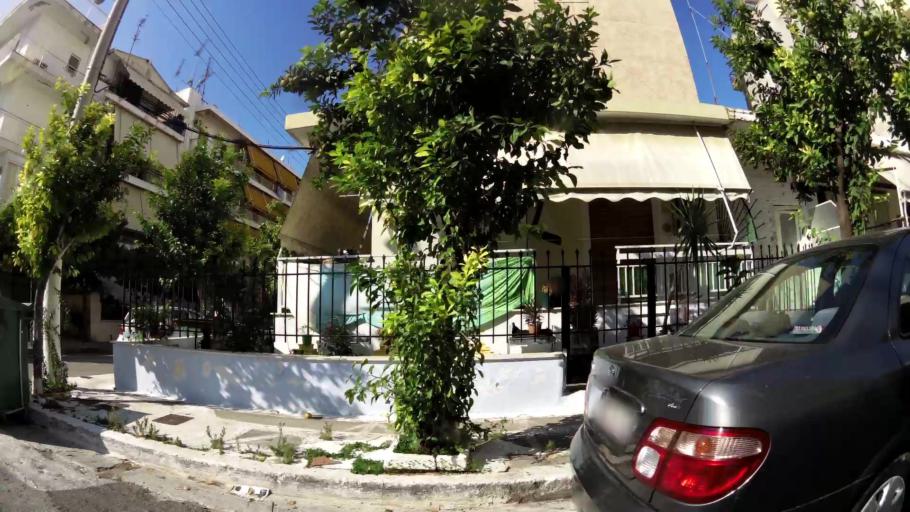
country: GR
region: Attica
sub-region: Nomos Piraios
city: Keratsini
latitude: 37.9661
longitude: 23.6212
